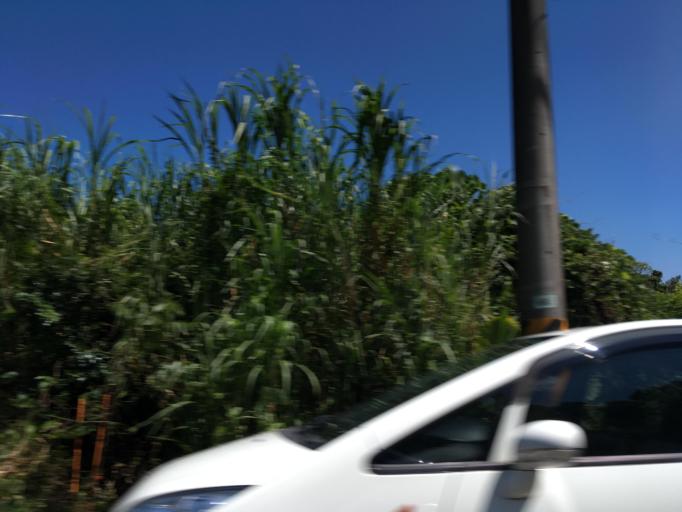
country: TW
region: Taipei
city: Taipei
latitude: 25.1481
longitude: 121.5050
